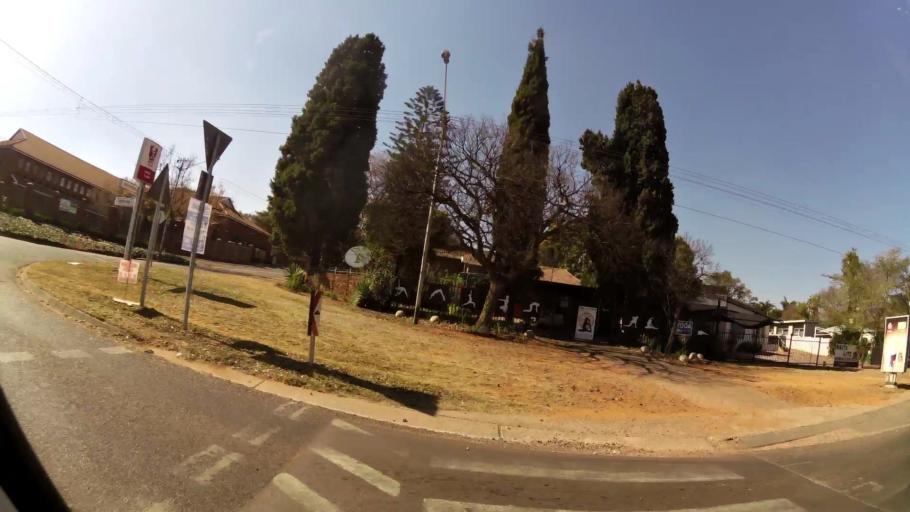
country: ZA
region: Gauteng
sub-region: City of Tshwane Metropolitan Municipality
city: Pretoria
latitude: -25.8020
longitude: 28.2345
